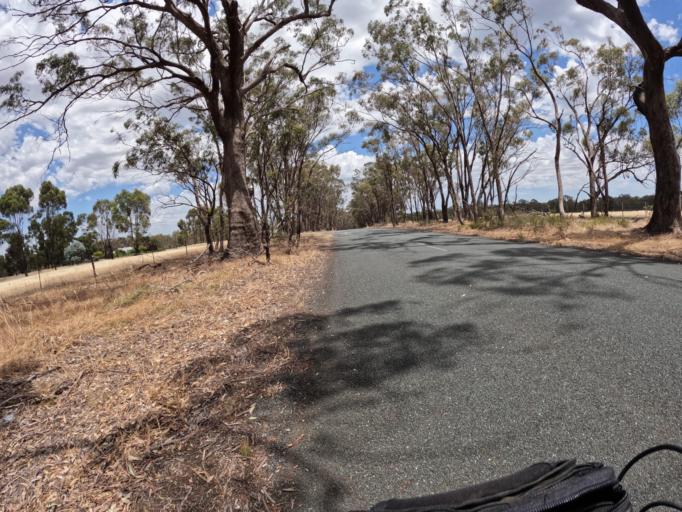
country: AU
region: Victoria
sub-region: Greater Shepparton
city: Shepparton
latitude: -36.6822
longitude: 145.1910
